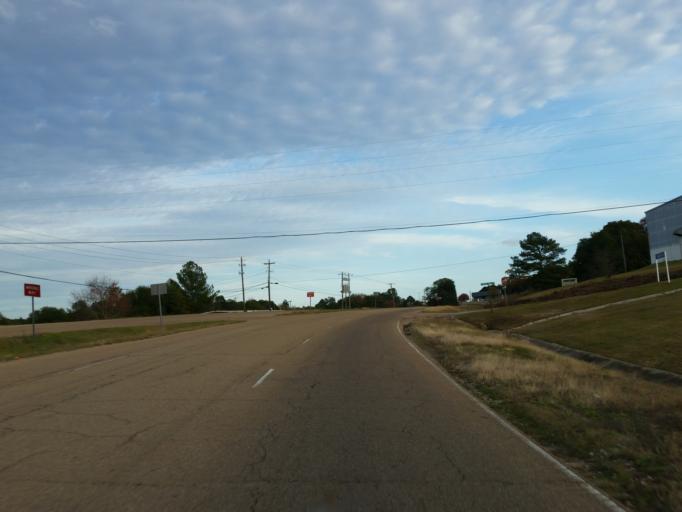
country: US
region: Mississippi
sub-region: Lauderdale County
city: Marion
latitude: 32.4126
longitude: -88.6333
